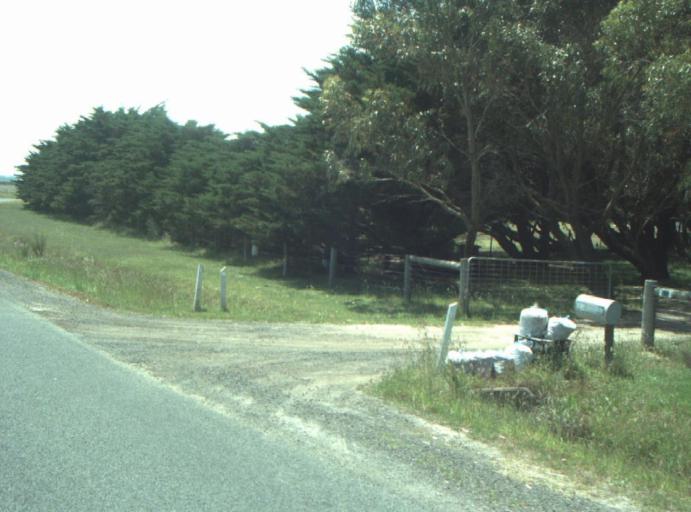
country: AU
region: Victoria
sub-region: Greater Geelong
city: Leopold
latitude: -38.2701
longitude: 144.4390
